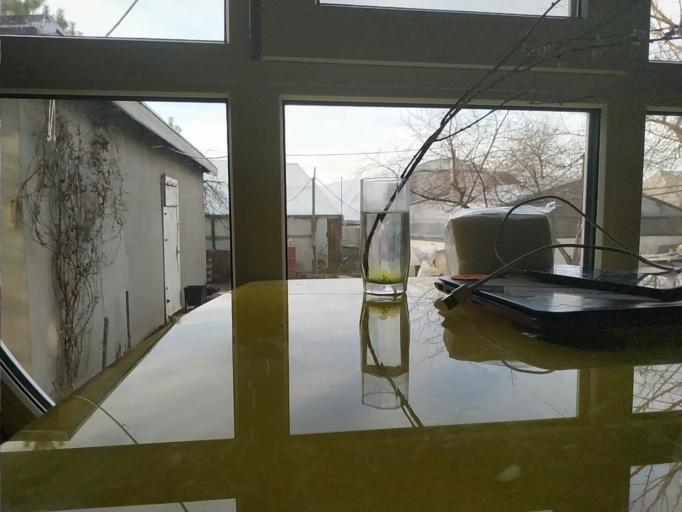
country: RU
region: Republic of Karelia
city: Suoyarvi
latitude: 61.8168
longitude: 32.2933
